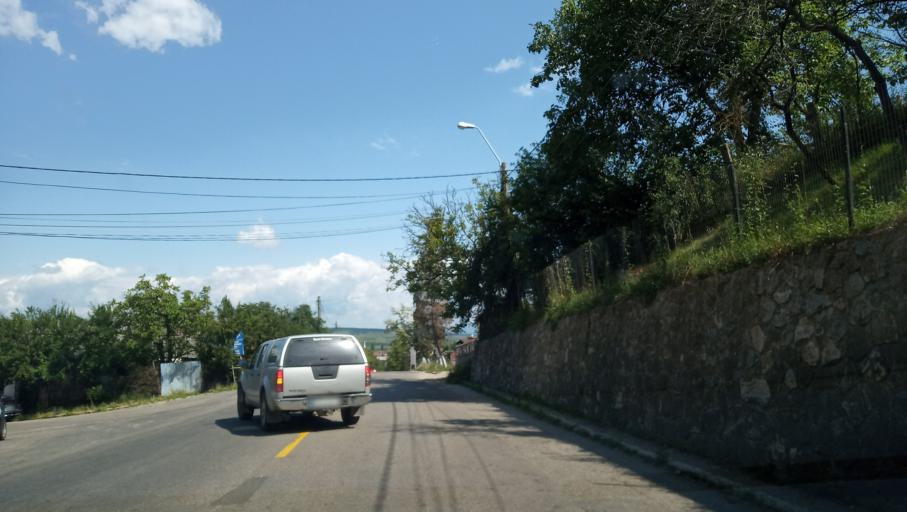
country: RO
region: Hunedoara
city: Hunedoara
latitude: 45.7420
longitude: 22.8989
